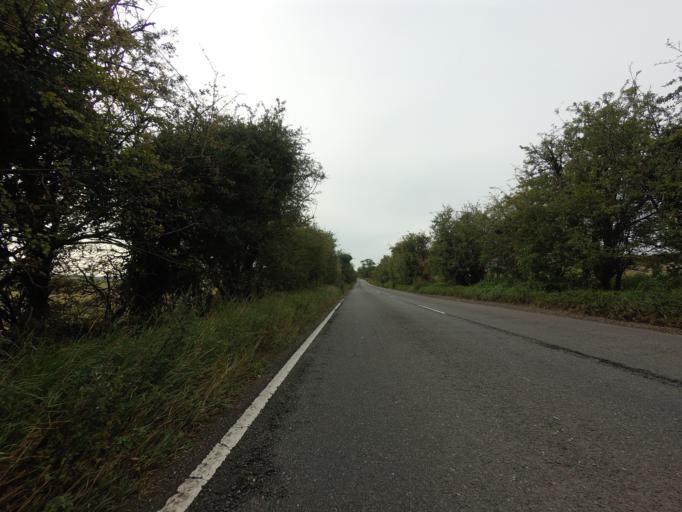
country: GB
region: England
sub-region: Cambridgeshire
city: Melbourn
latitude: 52.0395
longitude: 0.0424
